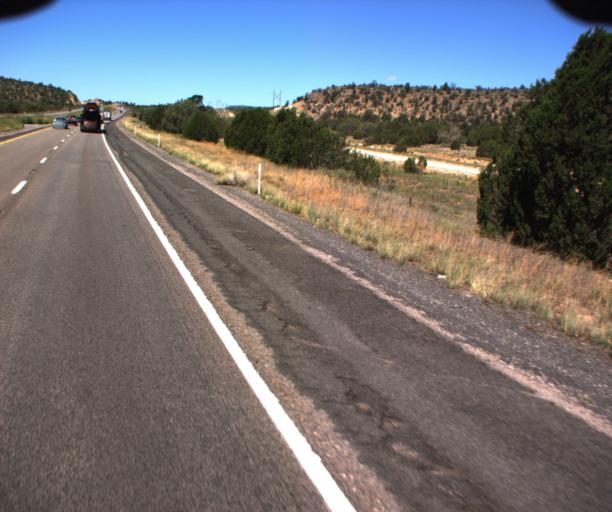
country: US
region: Arizona
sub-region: Mohave County
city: Peach Springs
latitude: 35.3028
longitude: -113.0053
